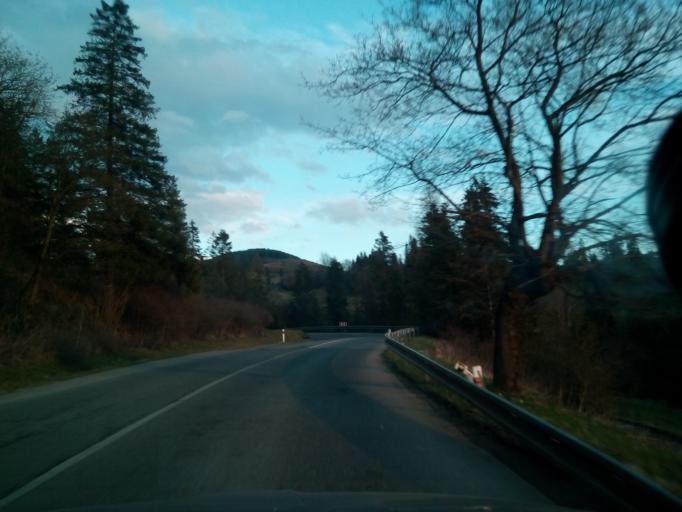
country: SK
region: Presovsky
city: Spisska Bela
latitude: 49.2921
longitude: 20.4111
